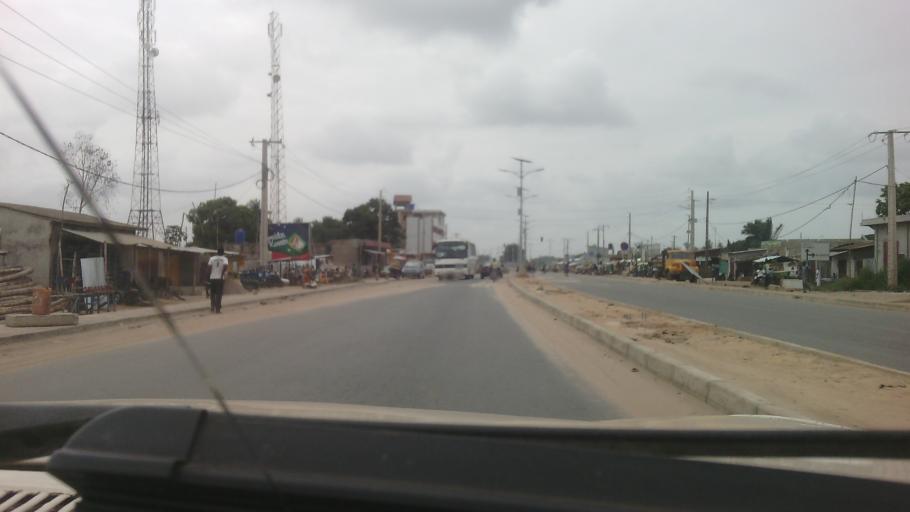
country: BJ
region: Atlantique
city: Hevie
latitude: 6.3854
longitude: 2.2082
